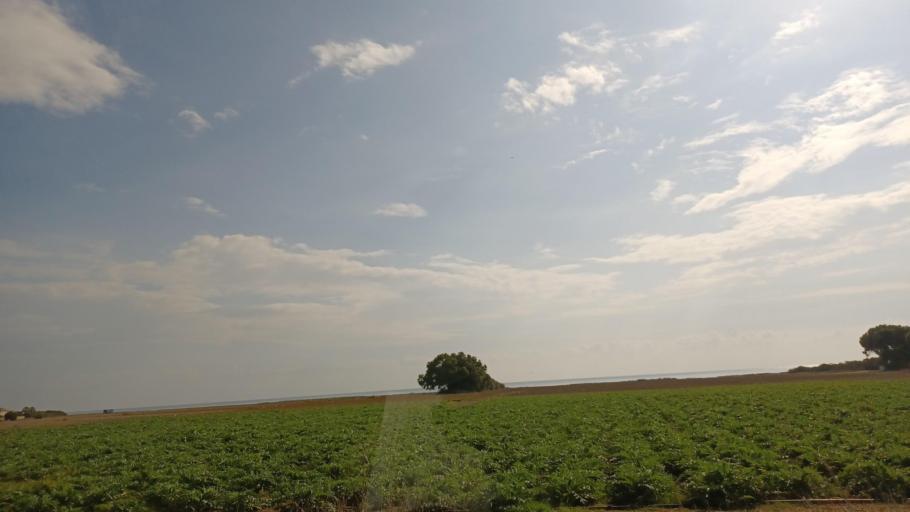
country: CY
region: Larnaka
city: Perivolia
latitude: 34.8243
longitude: 33.5696
